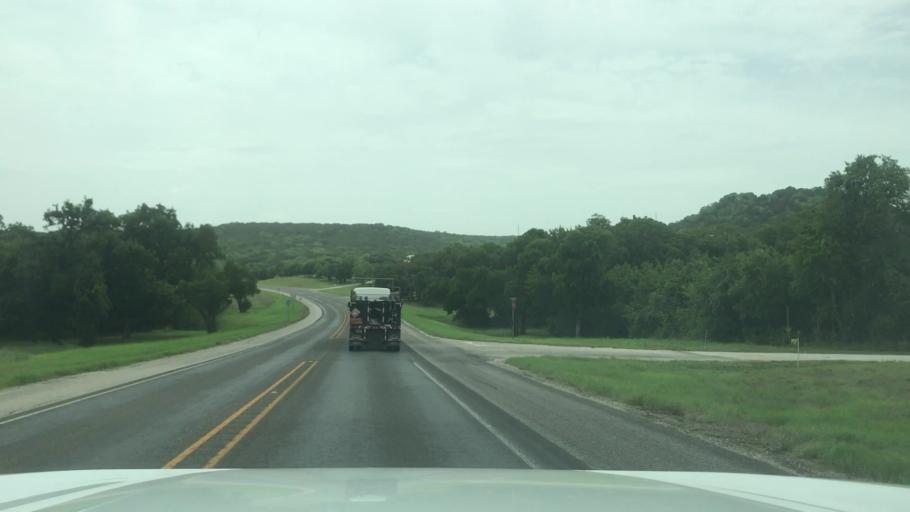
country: US
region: Texas
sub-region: Bosque County
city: Meridian
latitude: 31.9074
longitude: -97.6611
